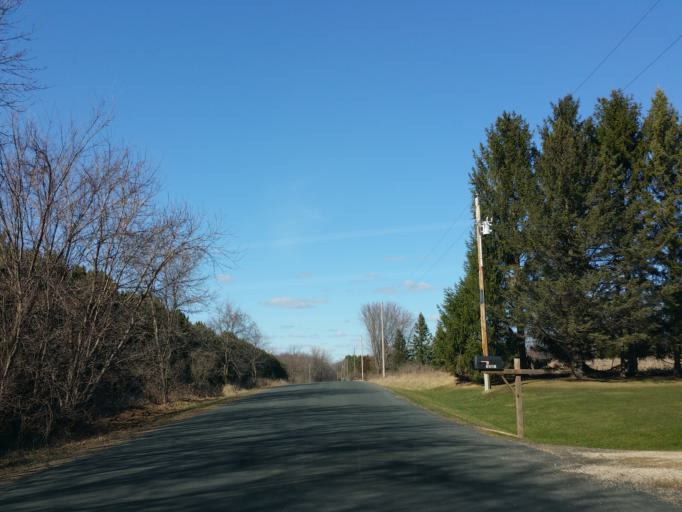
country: US
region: Minnesota
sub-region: Washington County
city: Stillwater
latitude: 45.0799
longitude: -92.7714
